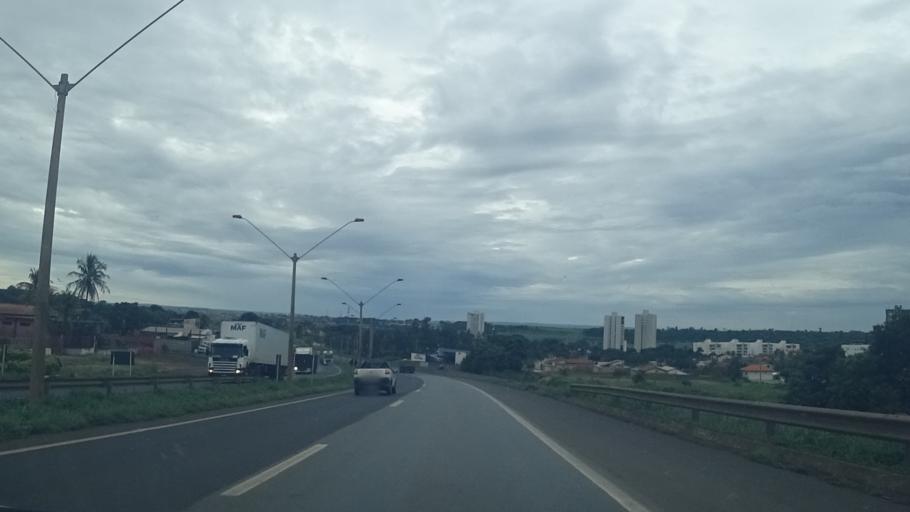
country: BR
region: Goias
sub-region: Itumbiara
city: Itumbiara
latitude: -18.4021
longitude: -49.2025
